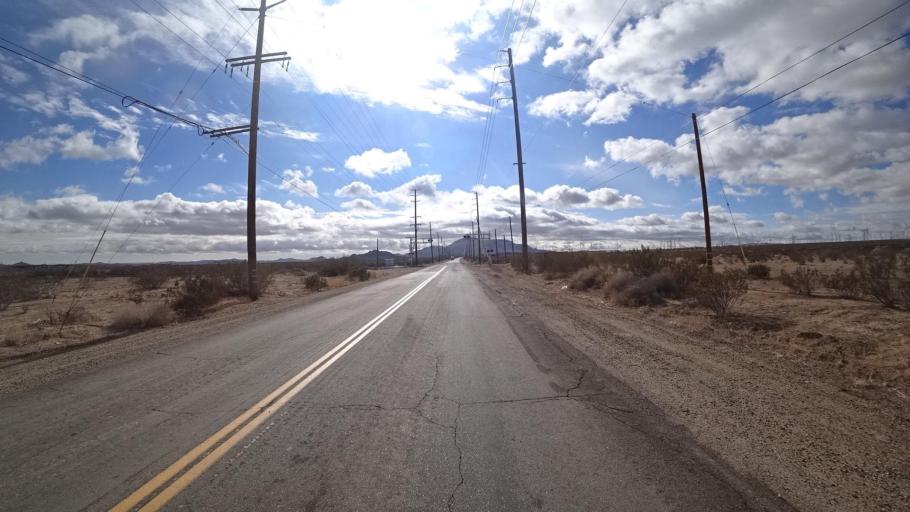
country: US
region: California
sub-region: Kern County
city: Mojave
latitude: 35.0471
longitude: -118.1854
